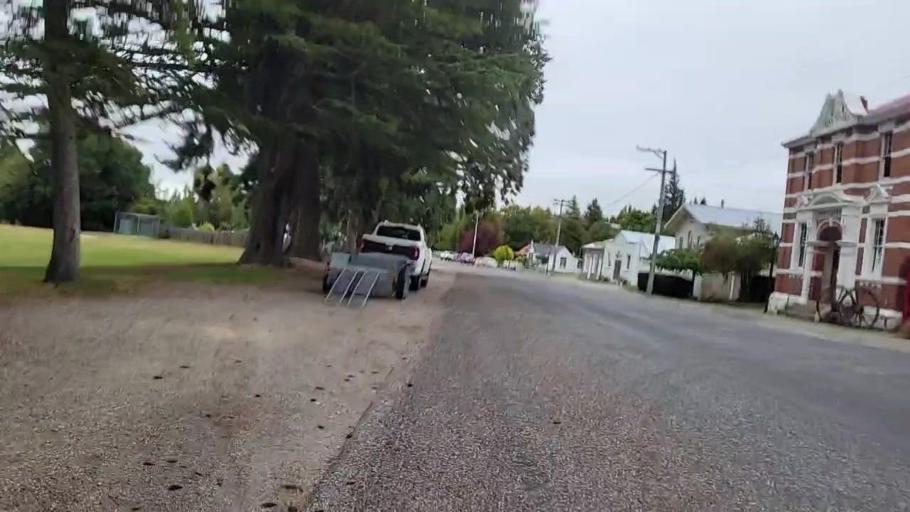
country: NZ
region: Otago
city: Oamaru
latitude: -45.0247
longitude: 170.1460
